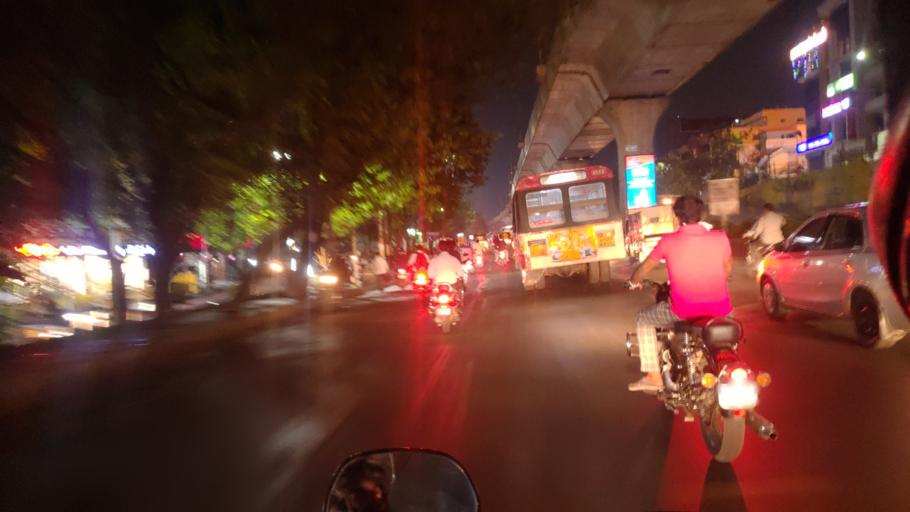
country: IN
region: Telangana
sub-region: Rangareddi
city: Gaddi Annaram
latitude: 17.3694
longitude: 78.5176
